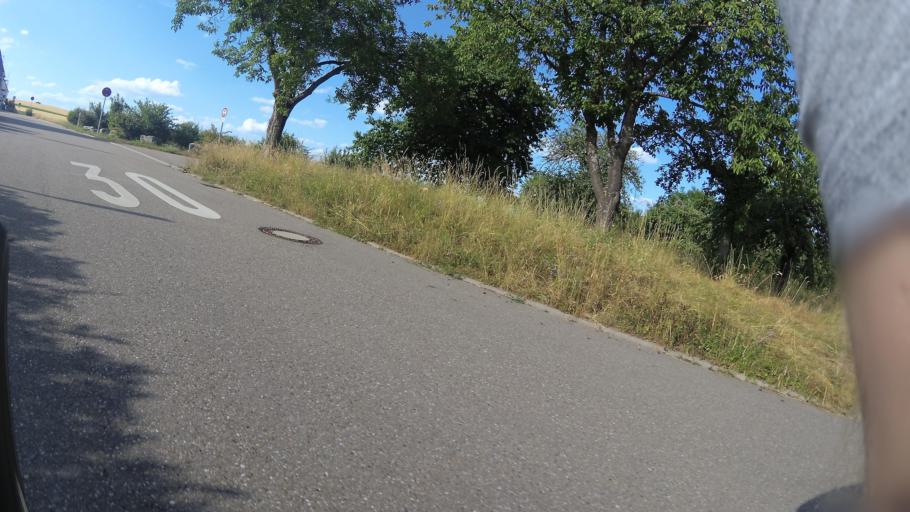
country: DE
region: Baden-Wuerttemberg
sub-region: Regierungsbezirk Stuttgart
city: Offenau
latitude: 49.2534
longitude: 9.1972
